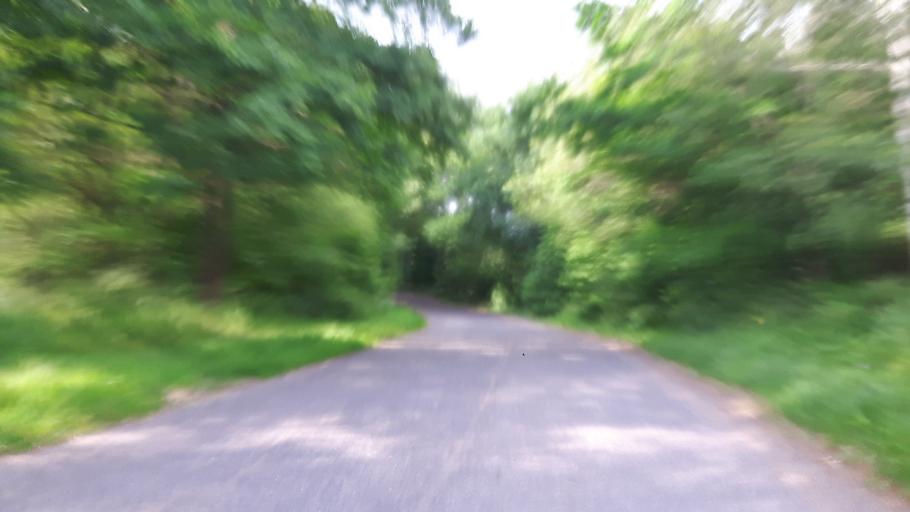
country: PL
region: West Pomeranian Voivodeship
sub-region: Powiat gryficki
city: Gryfice
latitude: 53.8311
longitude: 15.1464
